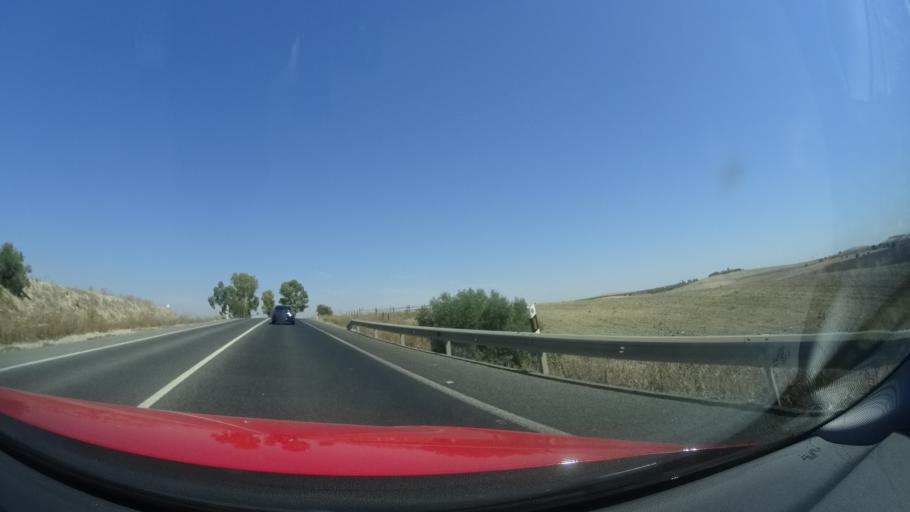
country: ES
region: Andalusia
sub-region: Provincia de Sevilla
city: Las Cabezas de San Juan
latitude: 36.9292
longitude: -5.9259
